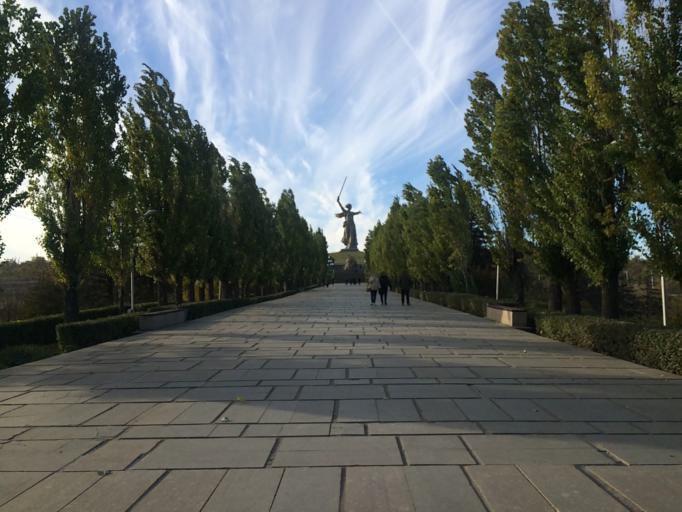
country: RU
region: Volgograd
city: Krasnoslobodsk
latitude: 48.7397
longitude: 44.5451
